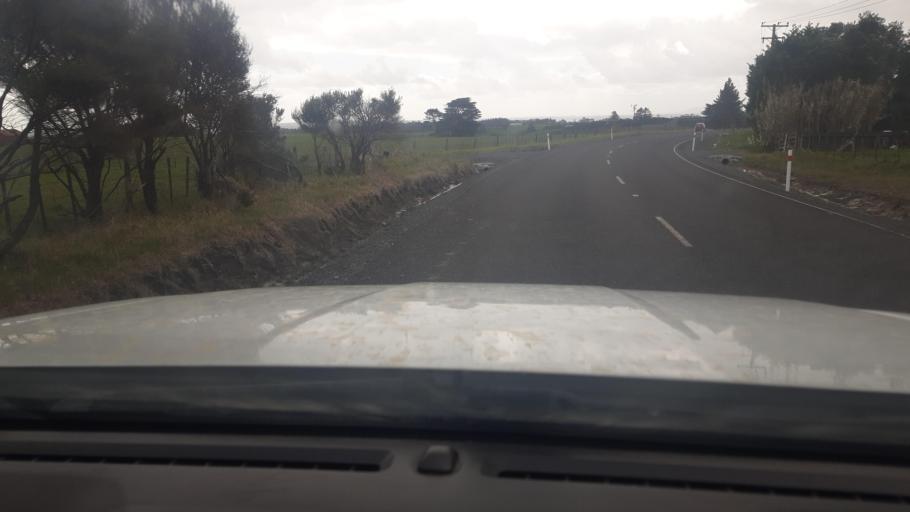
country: NZ
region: Northland
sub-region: Far North District
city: Kaitaia
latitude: -35.0470
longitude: 173.3197
